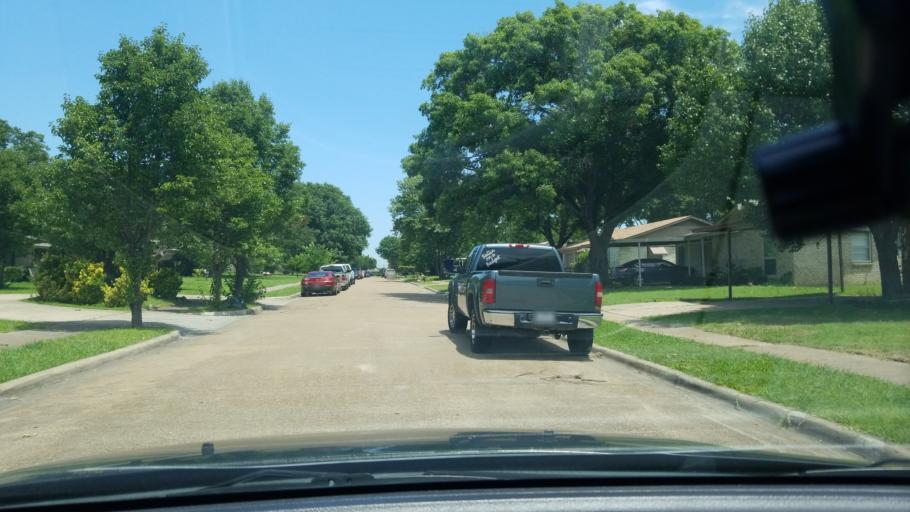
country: US
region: Texas
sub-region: Dallas County
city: Mesquite
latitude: 32.8035
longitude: -96.6582
